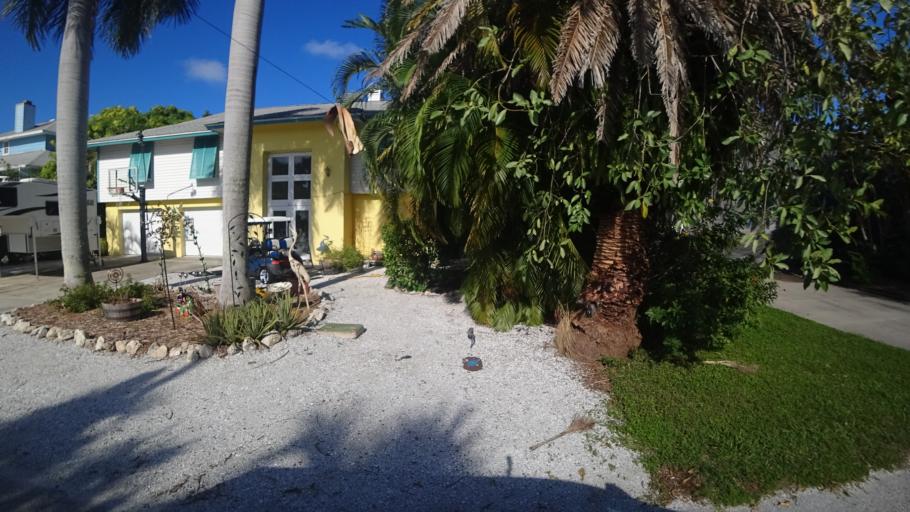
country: US
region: Florida
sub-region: Manatee County
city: Anna Maria
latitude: 27.5283
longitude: -82.7295
